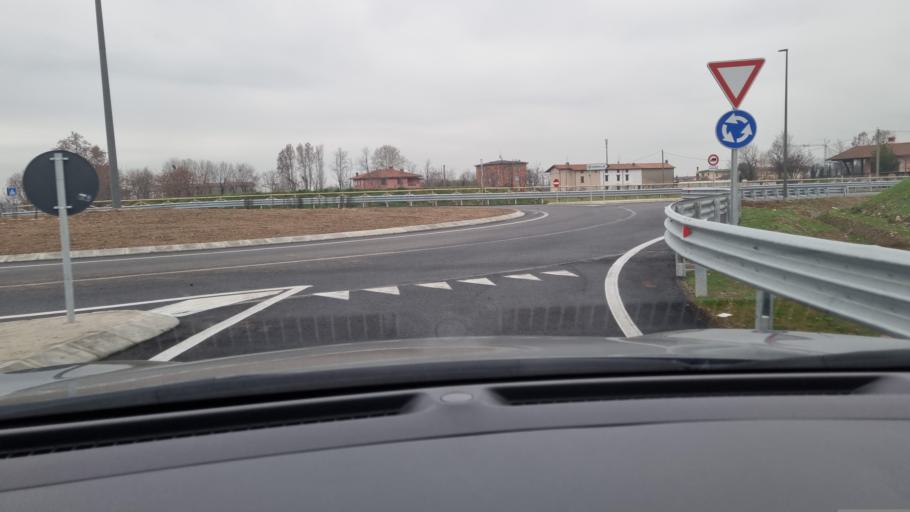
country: IT
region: Lombardy
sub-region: Provincia di Bergamo
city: Verdello
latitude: 45.6053
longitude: 9.6412
